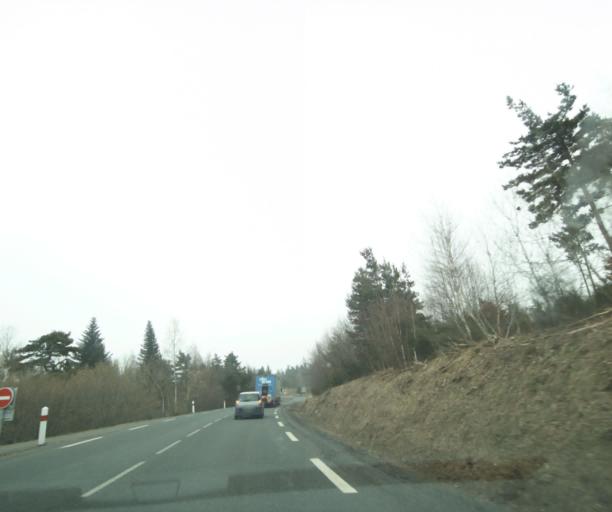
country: FR
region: Languedoc-Roussillon
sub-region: Departement de la Lozere
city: Langogne
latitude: 44.6925
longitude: 3.8128
